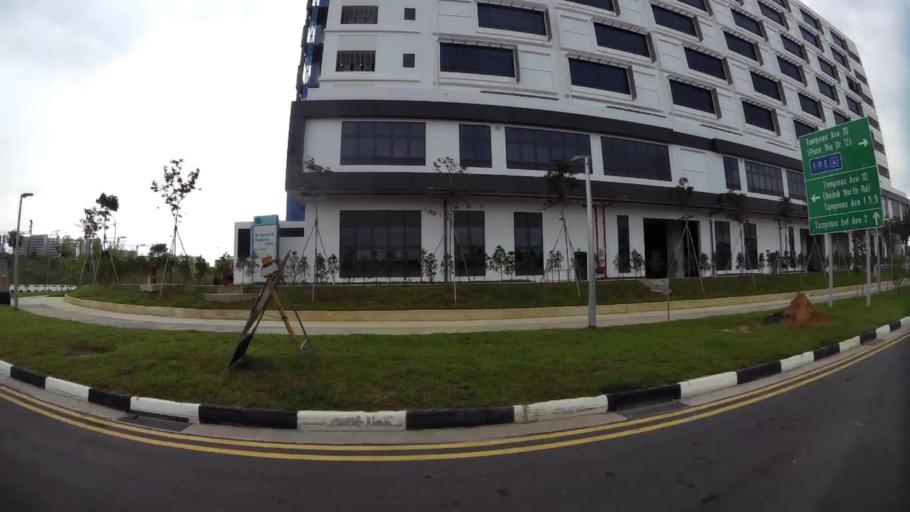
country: SG
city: Singapore
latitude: 1.3660
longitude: 103.9321
